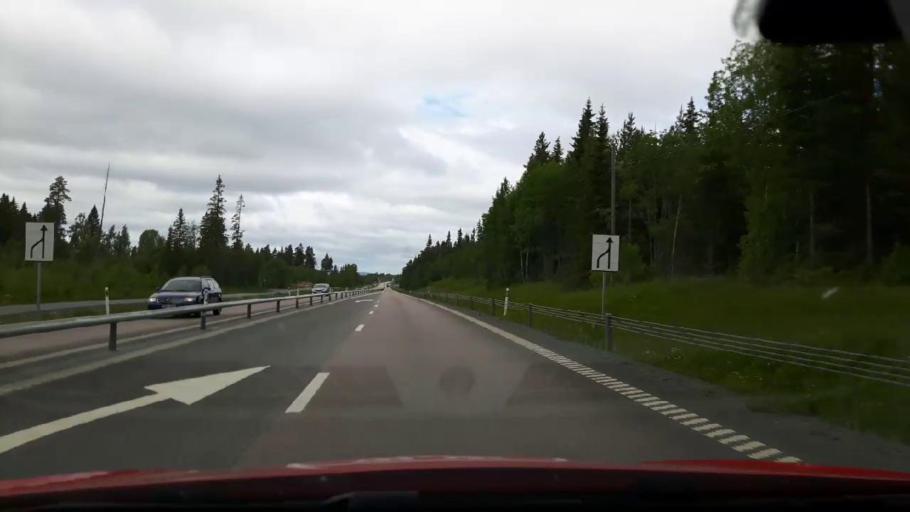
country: SE
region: Jaemtland
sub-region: Krokoms Kommun
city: Krokom
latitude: 63.2772
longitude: 14.5289
